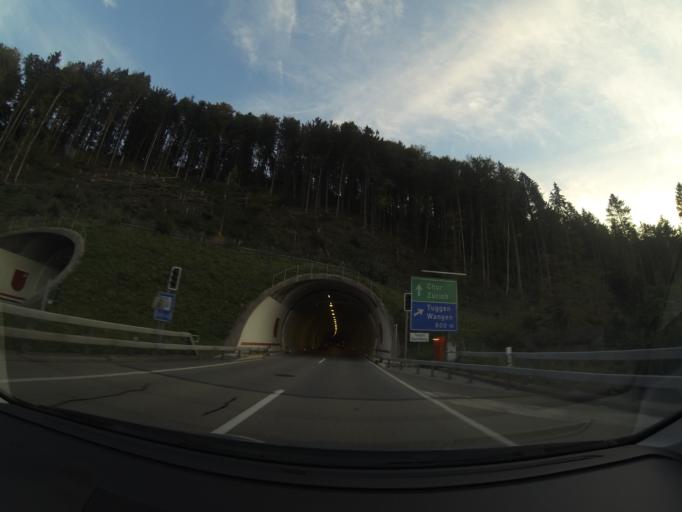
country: CH
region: Saint Gallen
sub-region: Wahlkreis See-Gaster
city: Schmerikon
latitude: 47.2162
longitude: 8.9619
